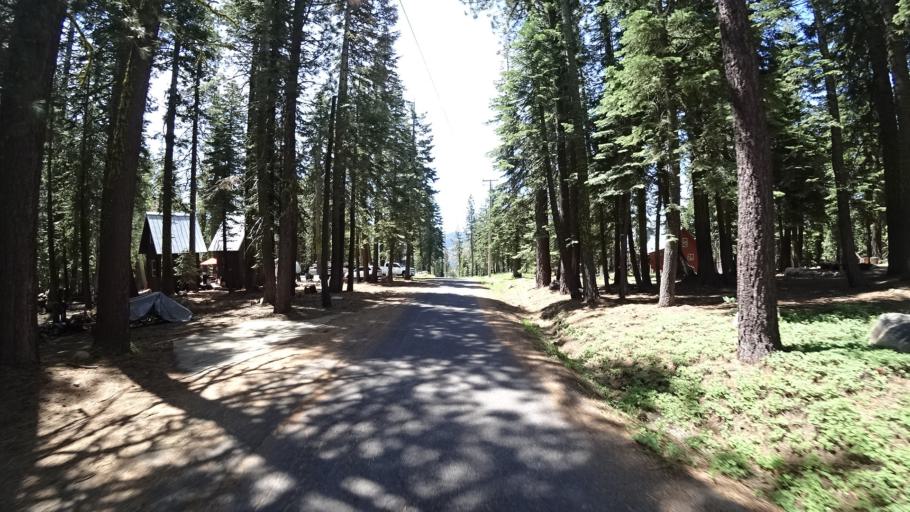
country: US
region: California
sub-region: Calaveras County
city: Arnold
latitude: 38.4281
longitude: -120.1014
